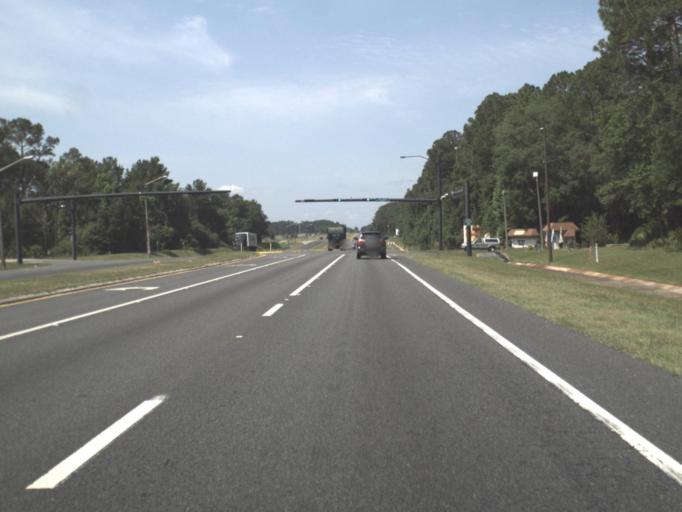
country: US
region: Florida
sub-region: Alachua County
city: Gainesville
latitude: 29.7008
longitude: -82.2786
